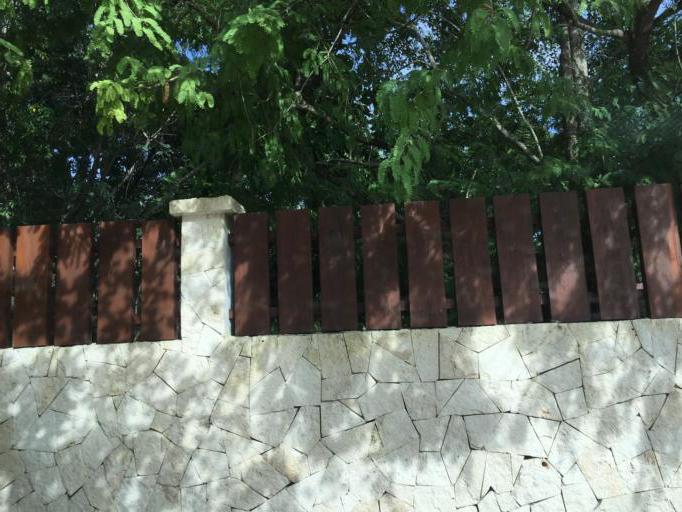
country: MX
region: Quintana Roo
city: Tulum
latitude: 20.2466
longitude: -87.4648
